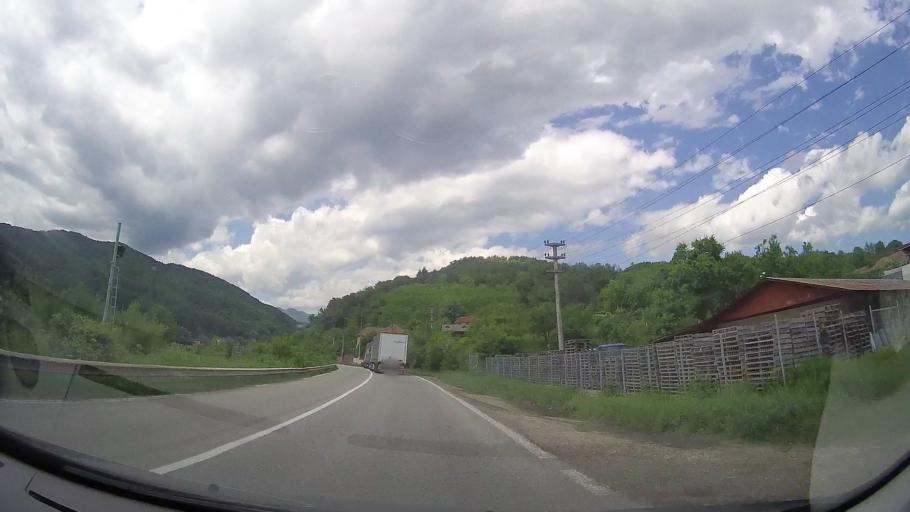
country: RO
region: Valcea
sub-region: Oras Calimanesti
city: Jiblea Veche
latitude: 45.2457
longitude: 24.3474
